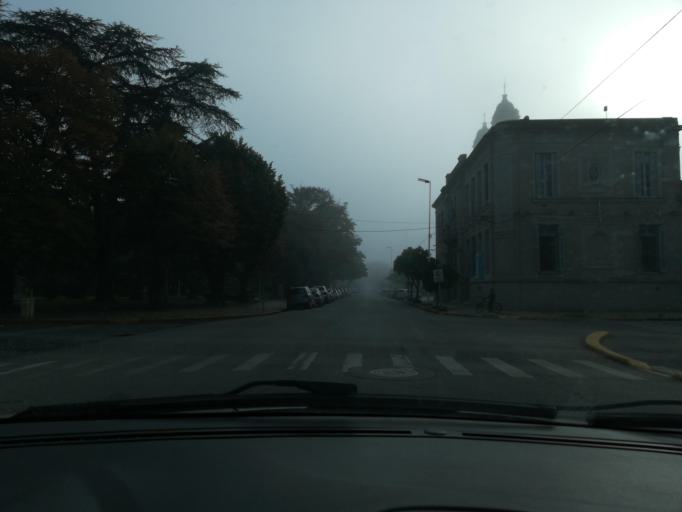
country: AR
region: Buenos Aires
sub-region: Partido de Balcarce
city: Balcarce
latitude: -37.8474
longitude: -58.2545
